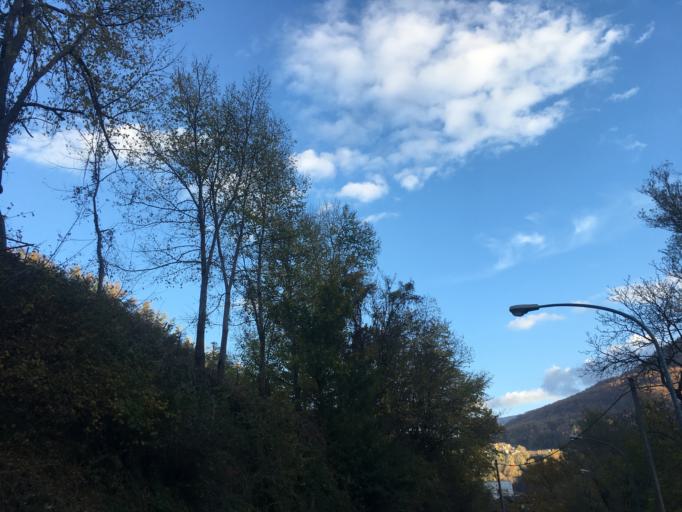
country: IT
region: The Marches
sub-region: Provincia di Ascoli Piceno
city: Arquata del Tronto
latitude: 42.7760
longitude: 13.2940
